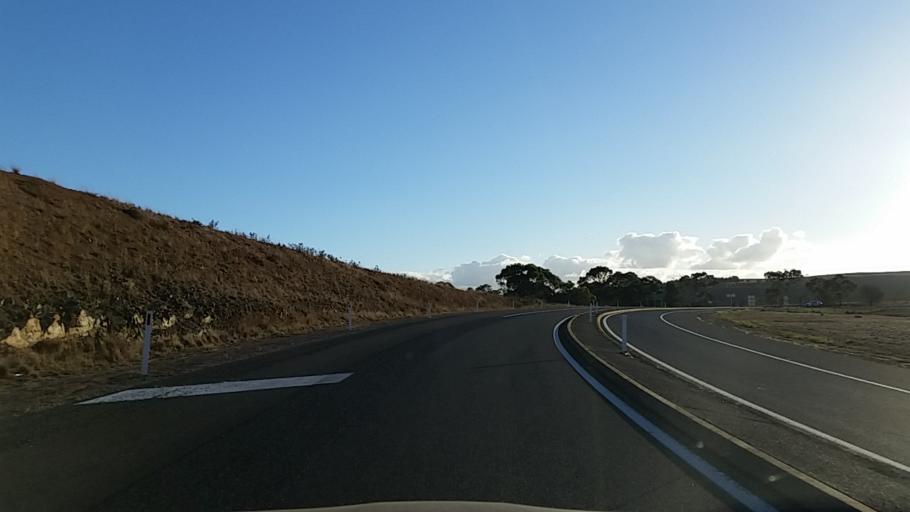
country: AU
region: South Australia
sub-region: Mount Barker
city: Callington
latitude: -35.1287
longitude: 139.0386
